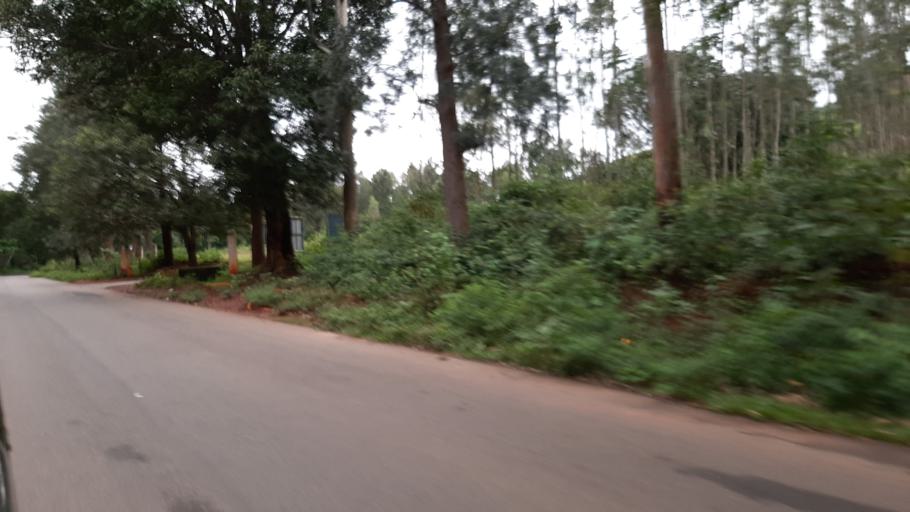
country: IN
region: Andhra Pradesh
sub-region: Vizianagaram District
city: Salur
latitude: 18.2884
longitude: 82.9309
